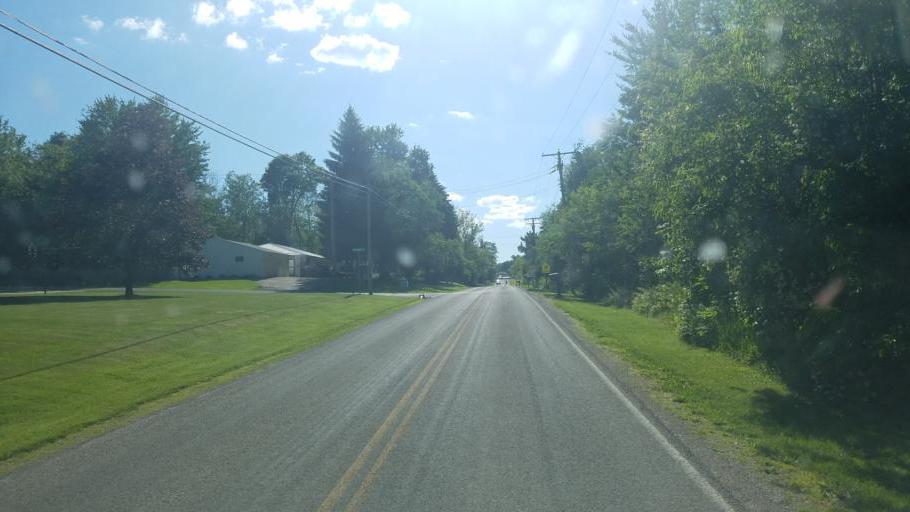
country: US
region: Ohio
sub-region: Richland County
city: Lincoln Heights
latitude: 40.7861
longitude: -82.4499
